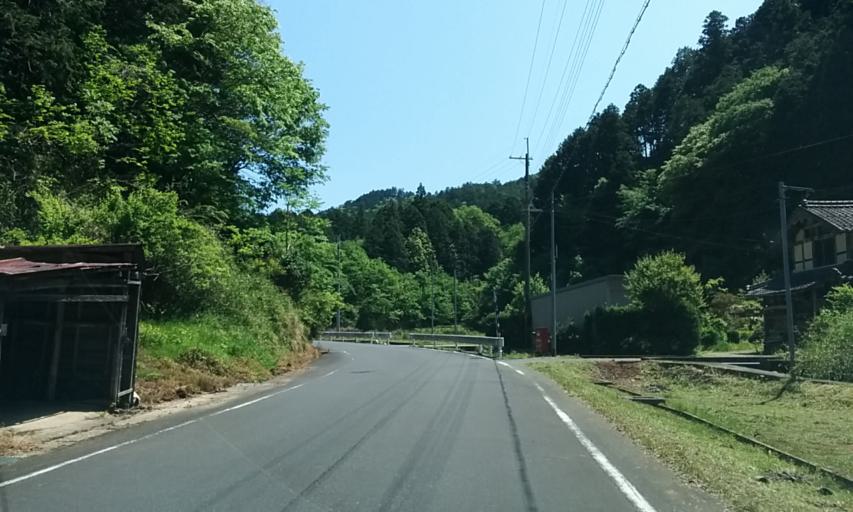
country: JP
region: Kyoto
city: Ayabe
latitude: 35.3838
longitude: 135.1847
